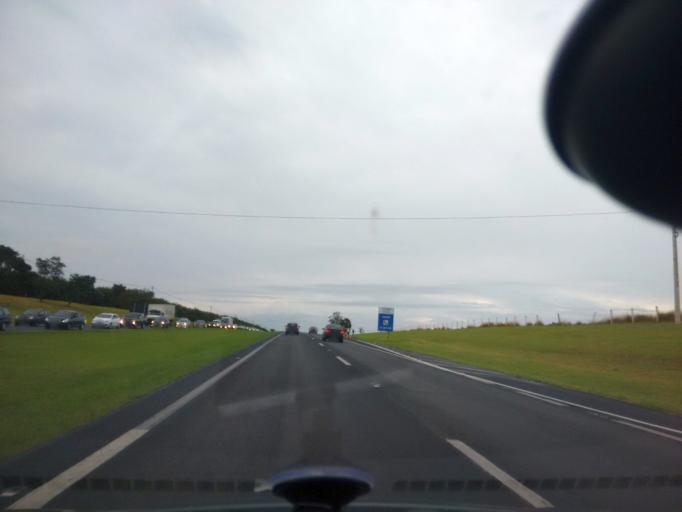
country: BR
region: Sao Paulo
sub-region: Itirapina
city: Itirapina
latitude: -22.2123
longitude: -47.7679
